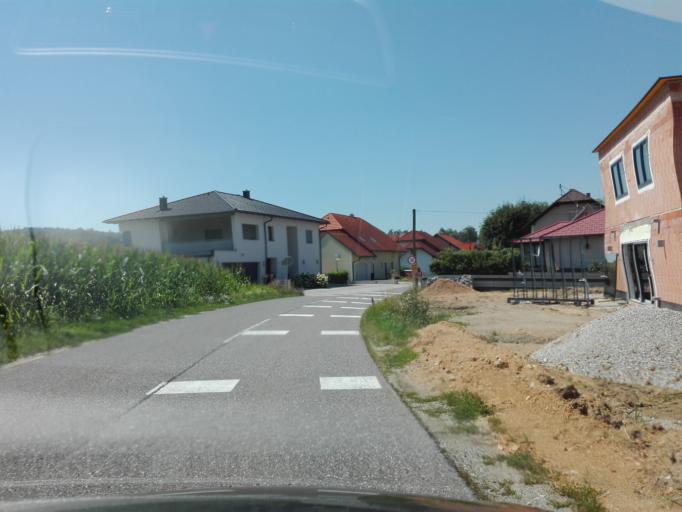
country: AT
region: Upper Austria
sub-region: Politischer Bezirk Urfahr-Umgebung
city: Gallneukirchen
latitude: 48.3299
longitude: 14.3812
